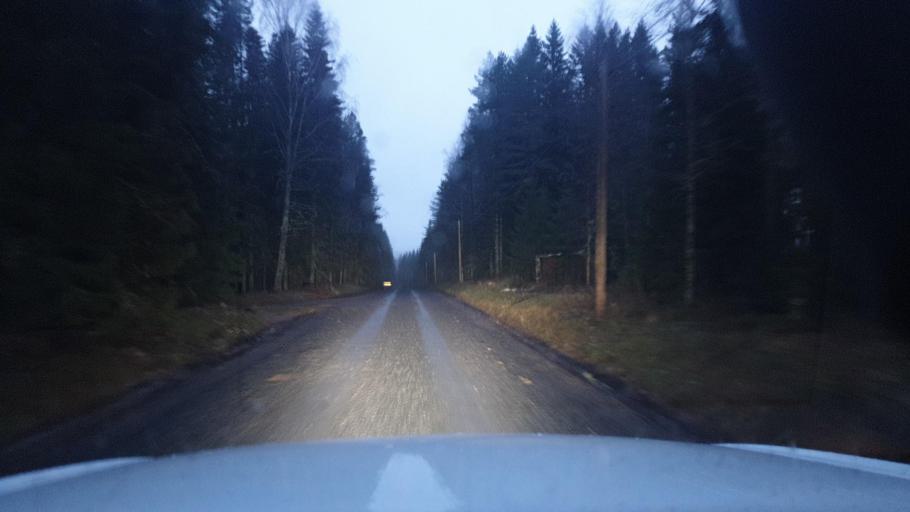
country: SE
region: Vaermland
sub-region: Eda Kommun
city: Charlottenberg
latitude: 60.1524
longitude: 12.5965
